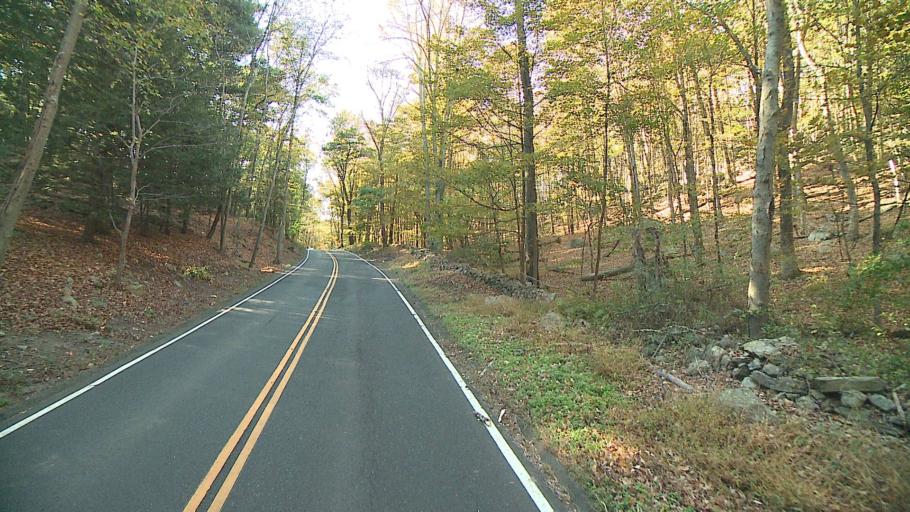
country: US
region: Connecticut
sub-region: Fairfield County
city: Georgetown
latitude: 41.2641
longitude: -73.3740
